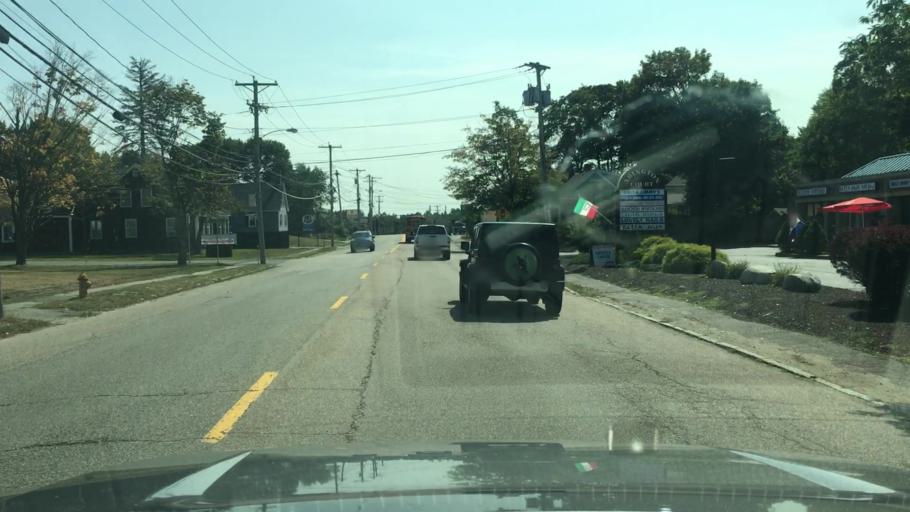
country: US
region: Massachusetts
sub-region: Plymouth County
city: Abington
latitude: 42.1317
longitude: -70.9501
